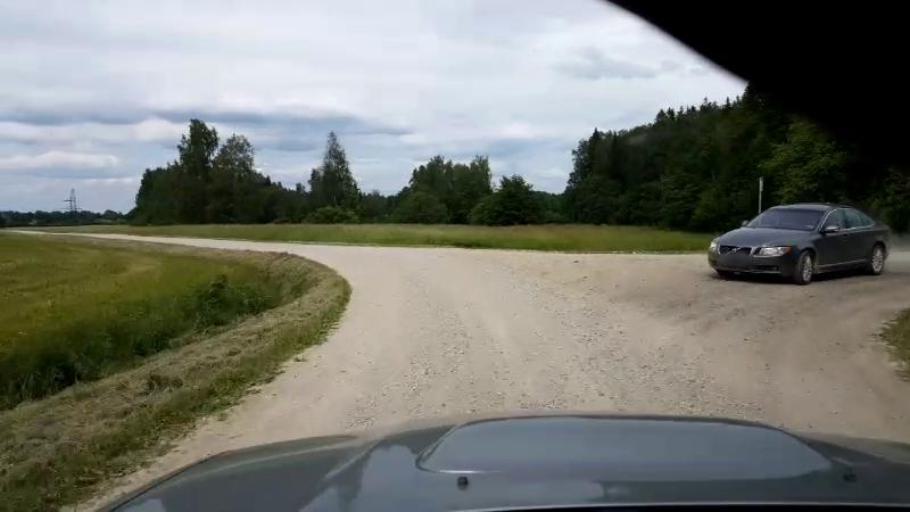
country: EE
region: Paernumaa
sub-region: Halinga vald
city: Parnu-Jaagupi
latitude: 58.5181
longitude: 24.5886
